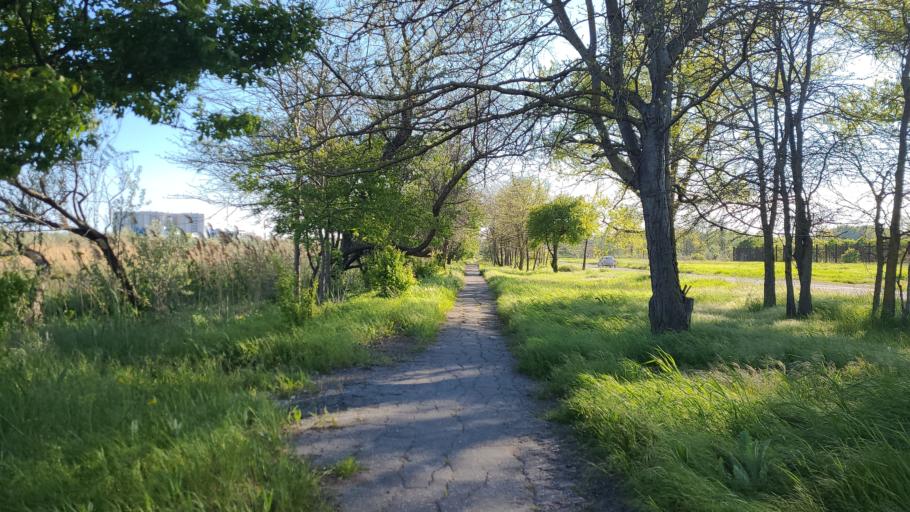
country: RU
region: Krasnodarskiy
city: Tsibanobalka
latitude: 44.9494
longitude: 37.3107
